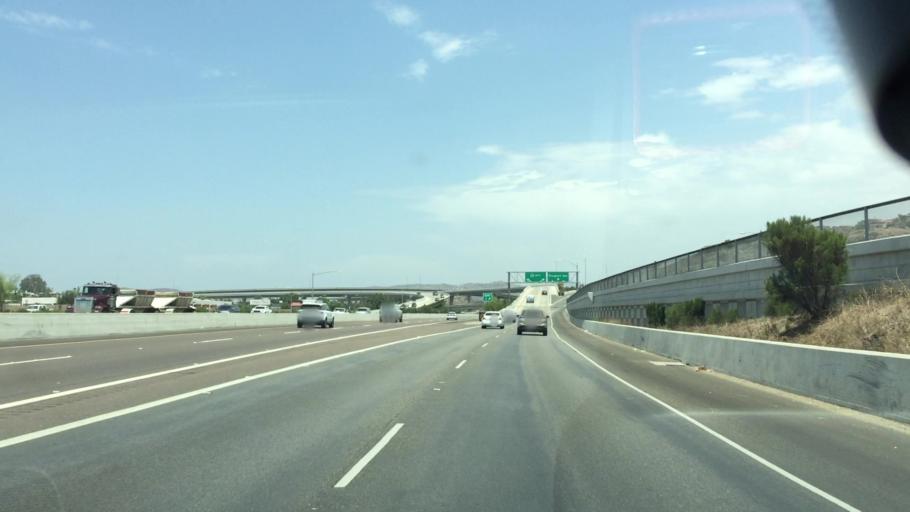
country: US
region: California
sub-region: San Diego County
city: Santee
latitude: 32.8260
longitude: -116.9617
